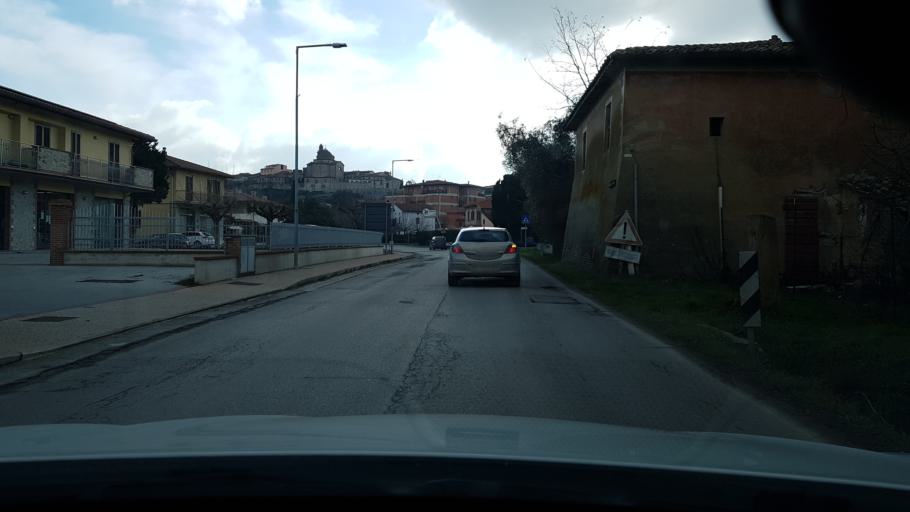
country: IT
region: Umbria
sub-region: Provincia di Perugia
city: Castiglione del Lago
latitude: 43.1296
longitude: 12.0439
